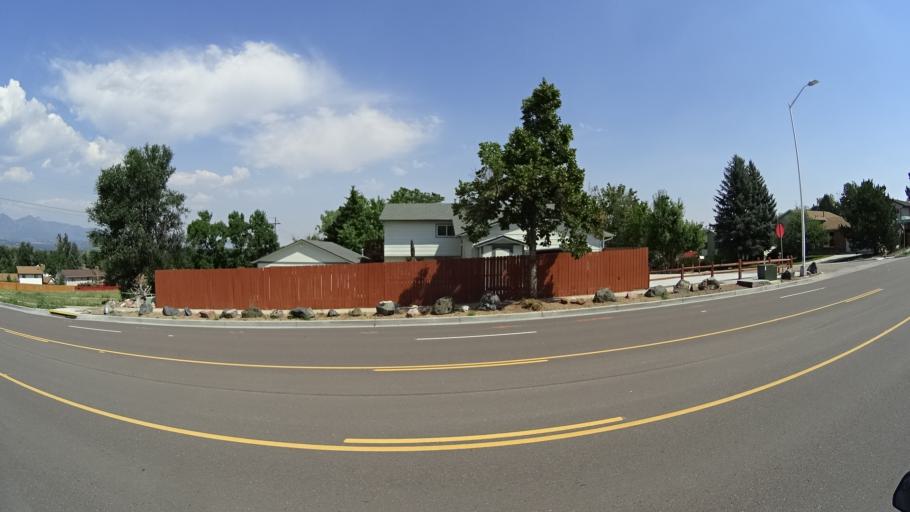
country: US
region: Colorado
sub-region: El Paso County
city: Colorado Springs
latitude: 38.9258
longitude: -104.7841
